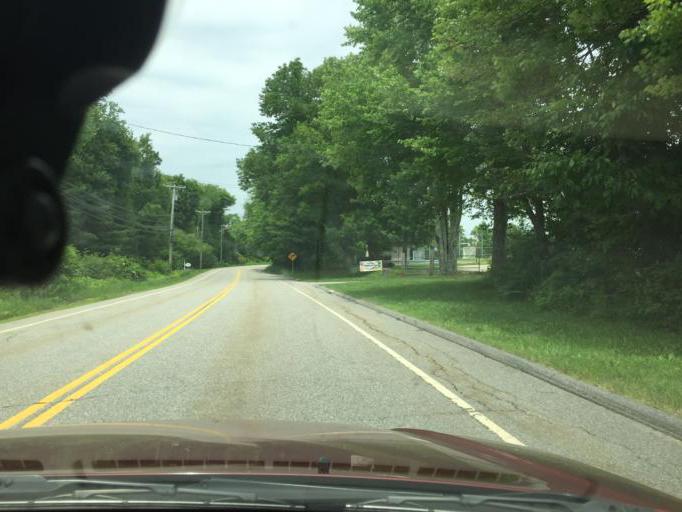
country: US
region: Connecticut
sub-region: Litchfield County
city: Litchfield
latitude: 41.7148
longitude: -73.2359
